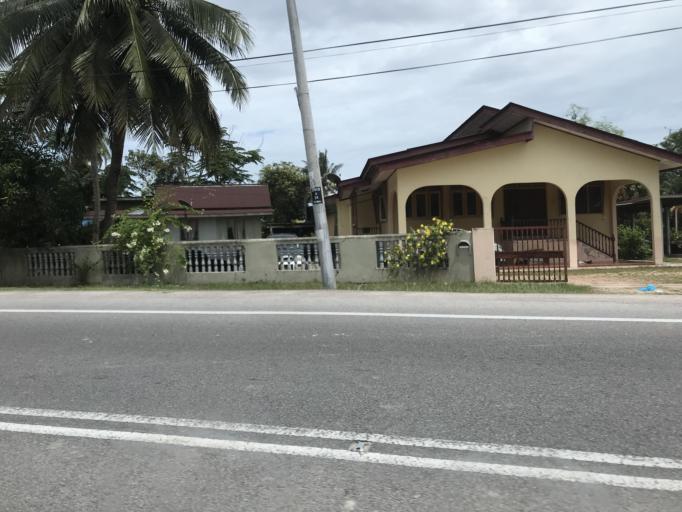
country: MY
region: Kelantan
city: Tumpat
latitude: 6.1732
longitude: 102.1840
